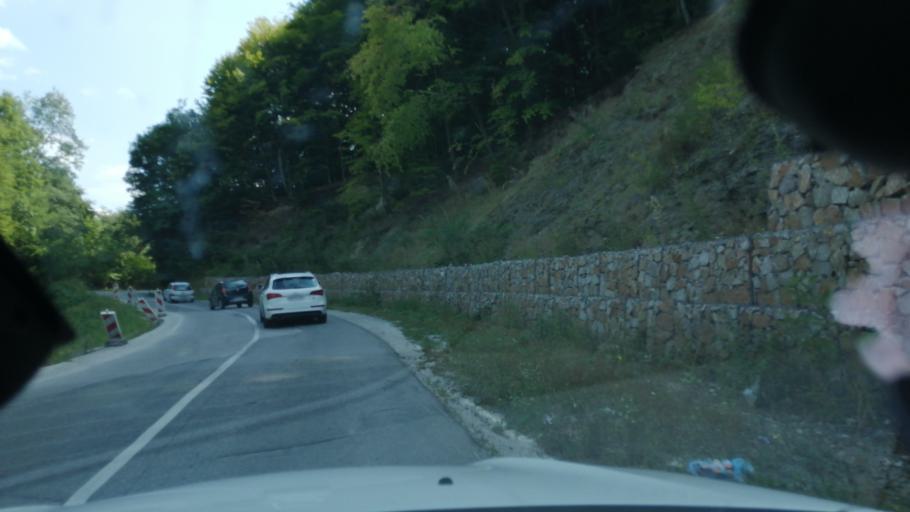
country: RS
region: Central Serbia
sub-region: Moravicki Okrug
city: Ivanjica
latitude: 43.6714
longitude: 20.2644
